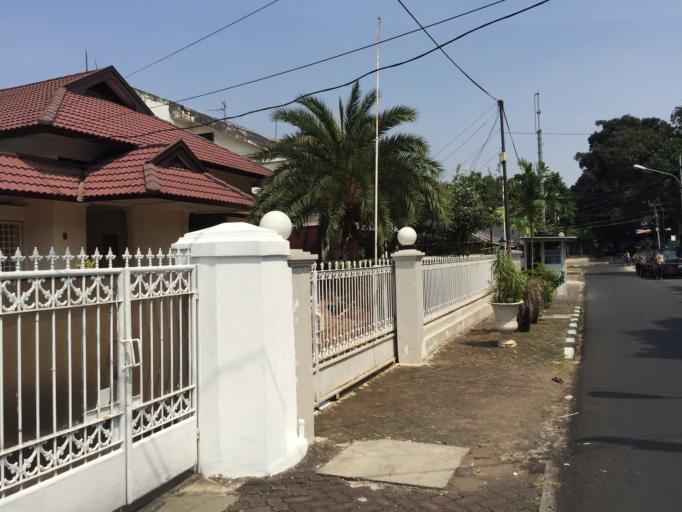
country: ID
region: Jakarta Raya
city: Jakarta
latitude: -6.2040
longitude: 106.8373
